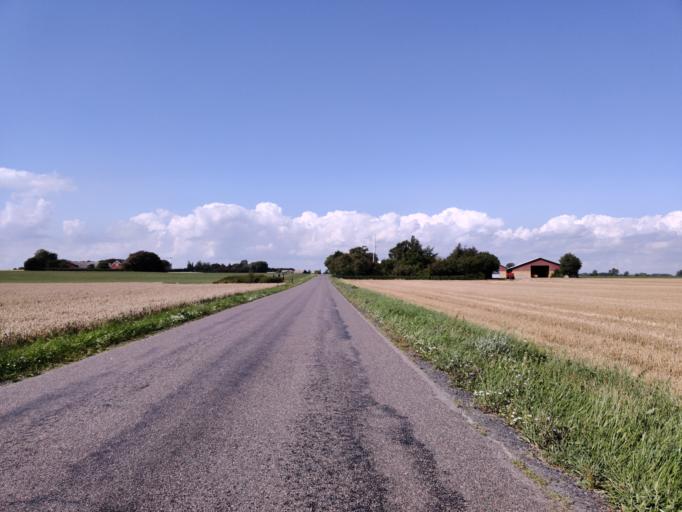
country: DK
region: Zealand
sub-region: Guldborgsund Kommune
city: Nykobing Falster
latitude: 54.6029
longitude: 11.9321
